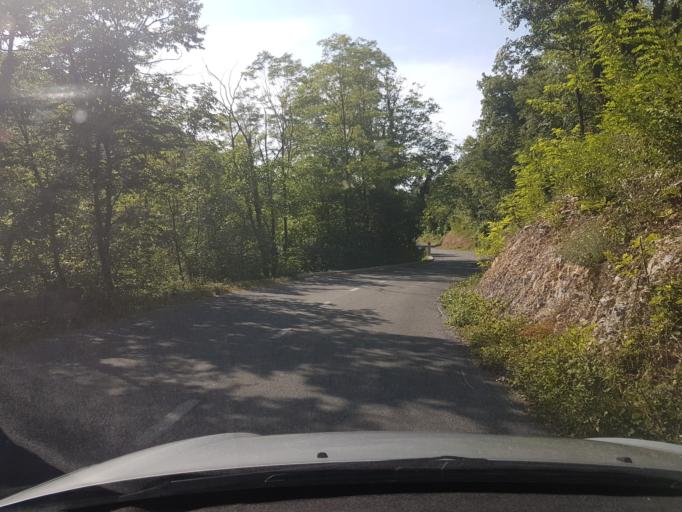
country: SI
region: Divaca
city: Divaca
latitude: 45.7546
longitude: 13.9410
